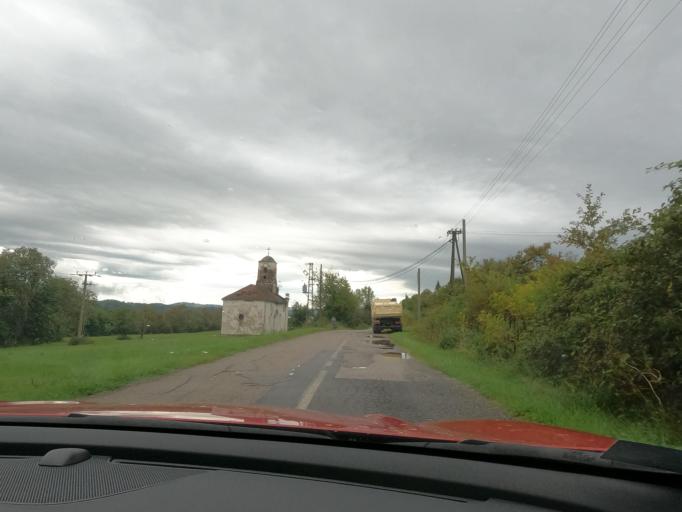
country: HR
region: Sisacko-Moslavacka
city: Glina
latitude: 45.3112
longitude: 16.1902
